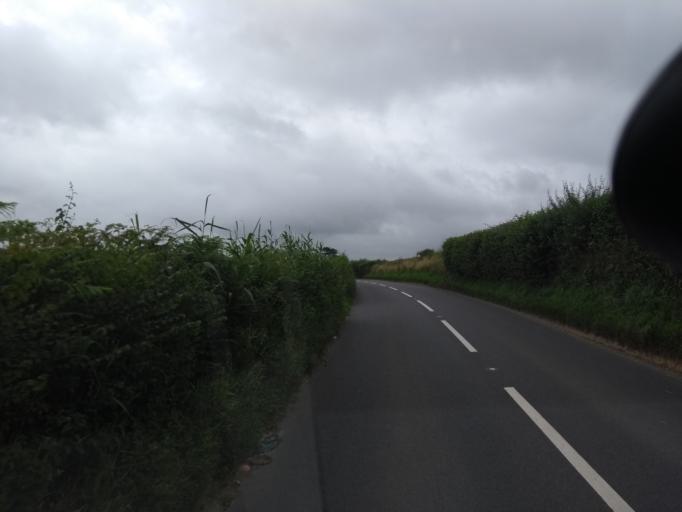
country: GB
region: England
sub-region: Somerset
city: Merriott
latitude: 50.9148
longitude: -2.7730
